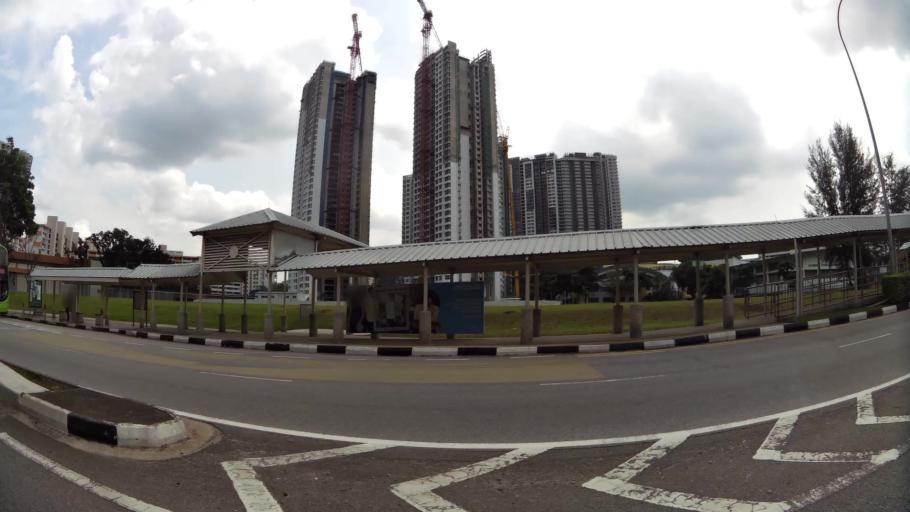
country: SG
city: Singapore
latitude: 1.3171
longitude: 103.7621
